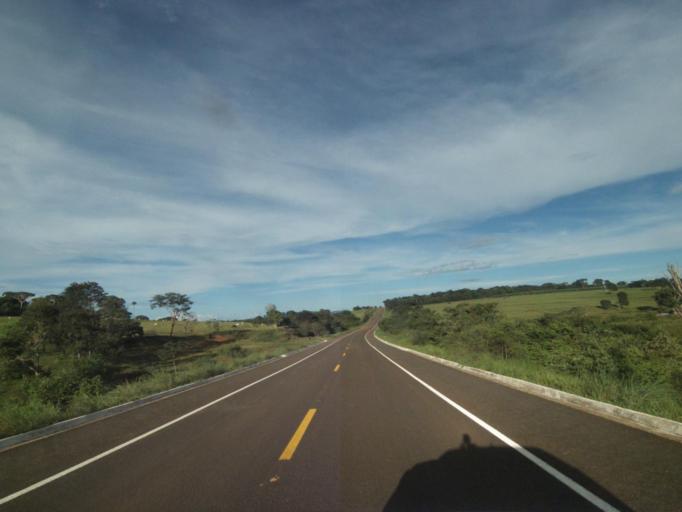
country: BR
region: Goias
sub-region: Jaragua
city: Jaragua
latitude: -15.8938
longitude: -49.4936
